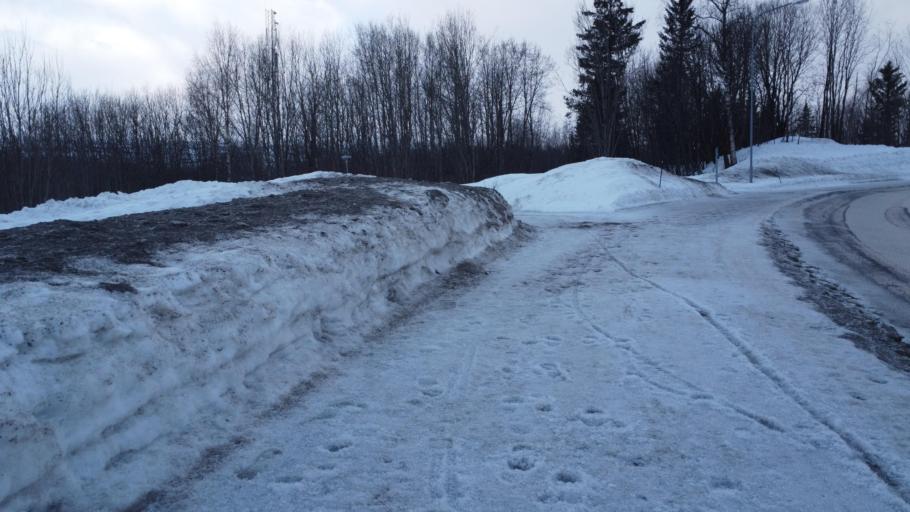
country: NO
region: Nordland
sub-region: Rana
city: Mo i Rana
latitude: 66.3271
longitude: 14.1582
